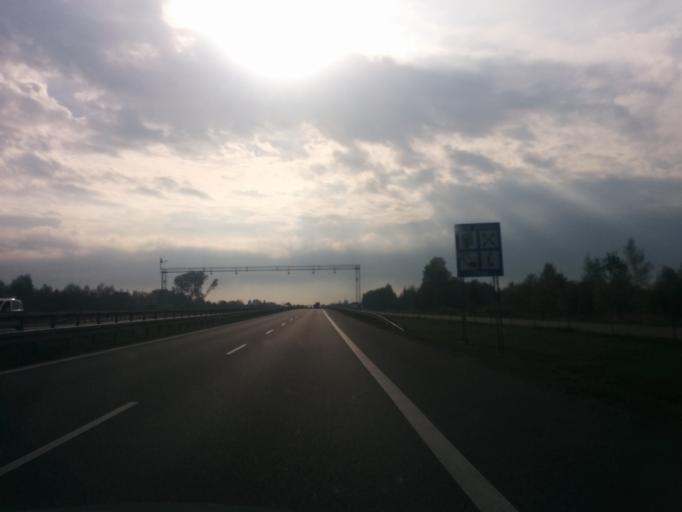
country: PL
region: Masovian Voivodeship
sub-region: Powiat bialobrzeski
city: Stara Blotnica
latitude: 51.5558
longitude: 21.0327
